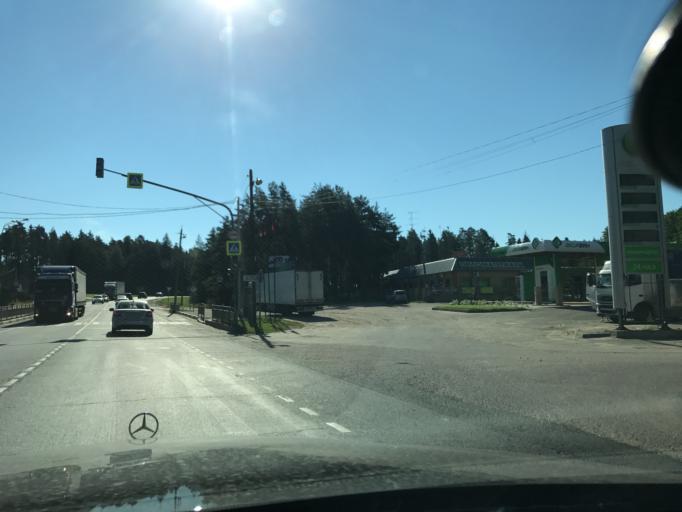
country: RU
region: Moskovskaya
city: Noginsk-9
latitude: 56.0989
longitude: 38.6654
